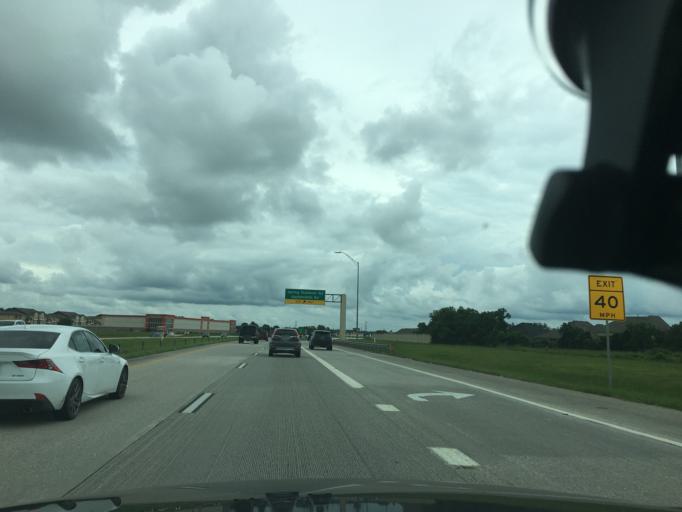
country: US
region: Texas
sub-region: Harris County
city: Tomball
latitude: 30.0809
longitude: -95.5384
